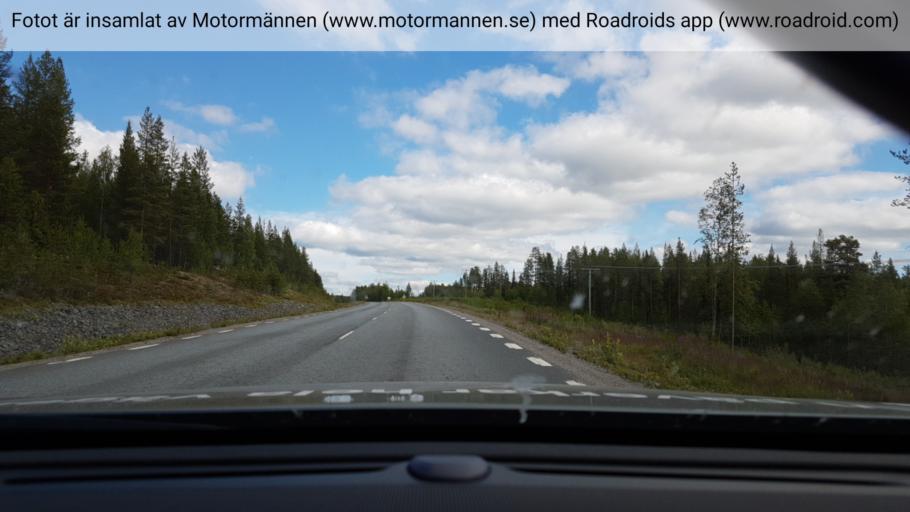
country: SE
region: Vaesterbotten
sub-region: Sorsele Kommun
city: Sorsele
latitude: 65.5375
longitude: 17.5801
